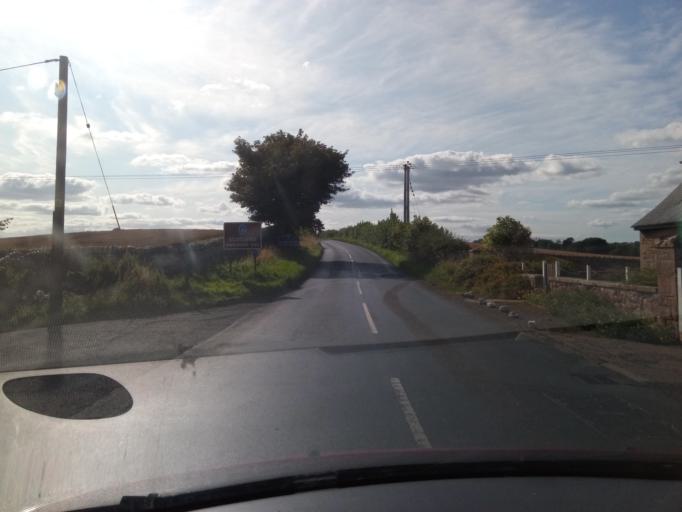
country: GB
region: England
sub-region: Northumberland
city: Berwick-Upon-Tweed
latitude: 55.7657
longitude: -2.0860
